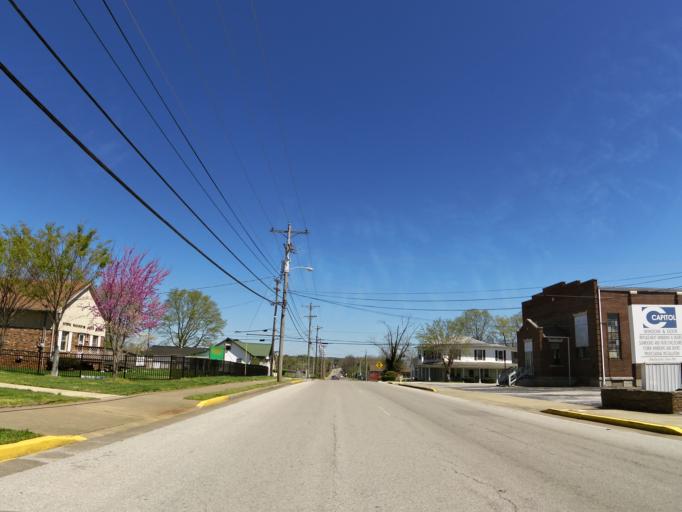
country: US
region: Kentucky
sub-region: Warren County
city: Bowling Green
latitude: 36.9984
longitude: -86.4319
